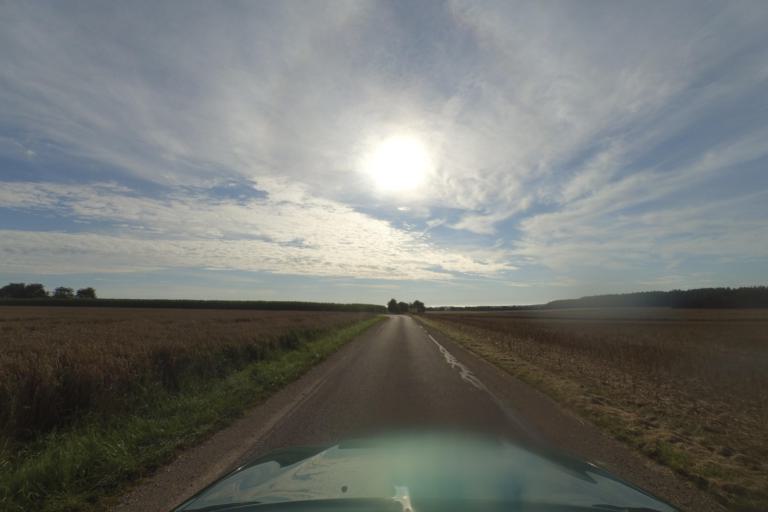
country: DE
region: Bavaria
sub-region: Upper Bavaria
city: Denkendorf
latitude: 48.9856
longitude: 11.5037
